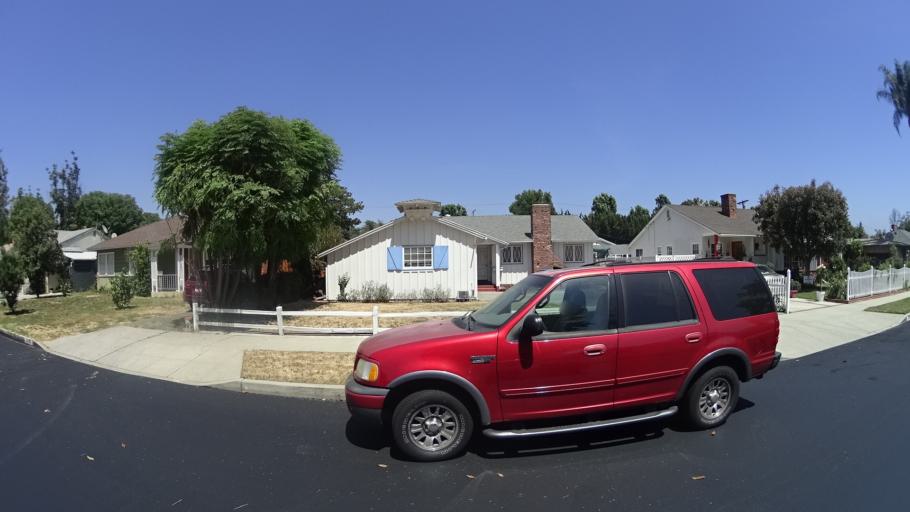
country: US
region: California
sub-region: Los Angeles County
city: Van Nuys
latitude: 34.1921
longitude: -118.4390
